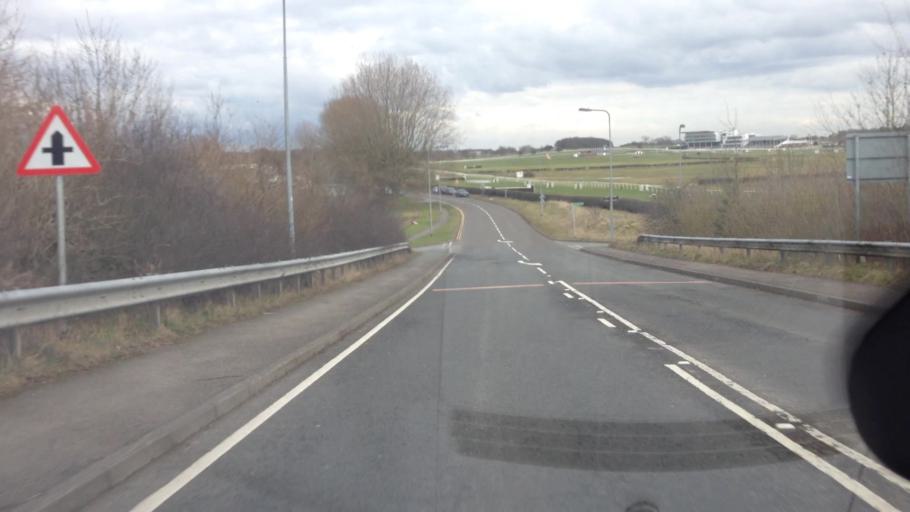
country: GB
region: England
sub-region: City and Borough of Leeds
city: Wetherby
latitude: 53.9345
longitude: -1.3732
